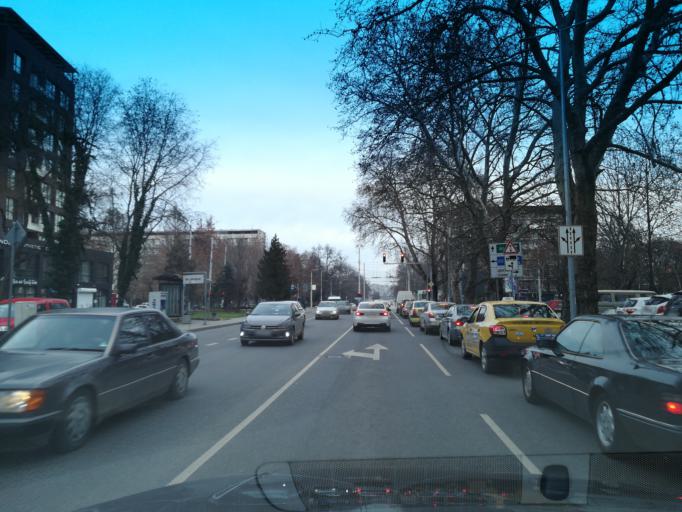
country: BG
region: Plovdiv
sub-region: Obshtina Plovdiv
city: Plovdiv
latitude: 42.1470
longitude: 24.7313
